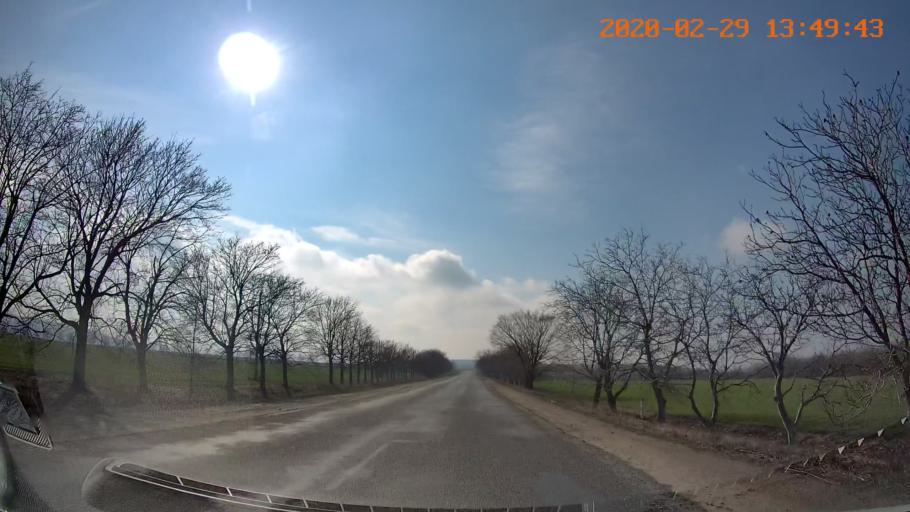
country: MD
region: Floresti
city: Leninskiy
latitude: 47.8413
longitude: 28.4803
